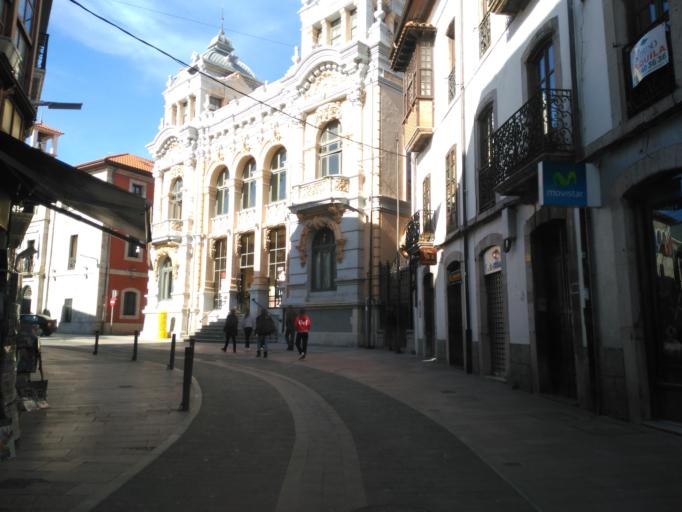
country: ES
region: Asturias
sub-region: Province of Asturias
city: Llanes
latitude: 43.4208
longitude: -4.7550
